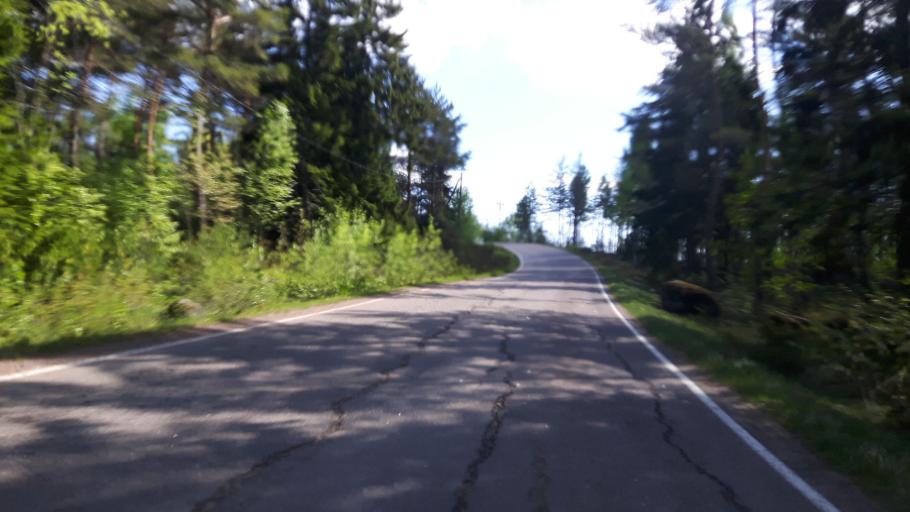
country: FI
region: Kymenlaakso
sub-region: Kotka-Hamina
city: Hamina
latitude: 60.5136
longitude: 27.4147
